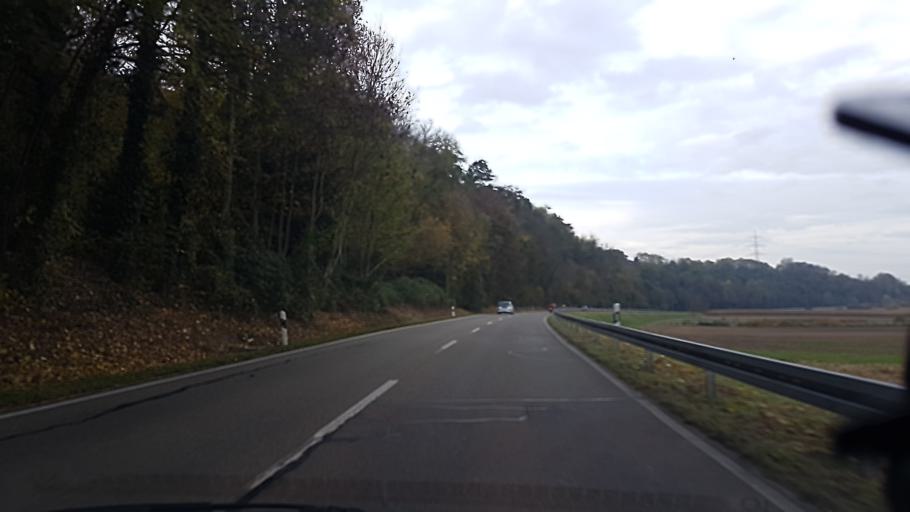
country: DE
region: Baden-Wuerttemberg
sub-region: Freiburg Region
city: Bahlingen
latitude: 48.1333
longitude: 7.7384
